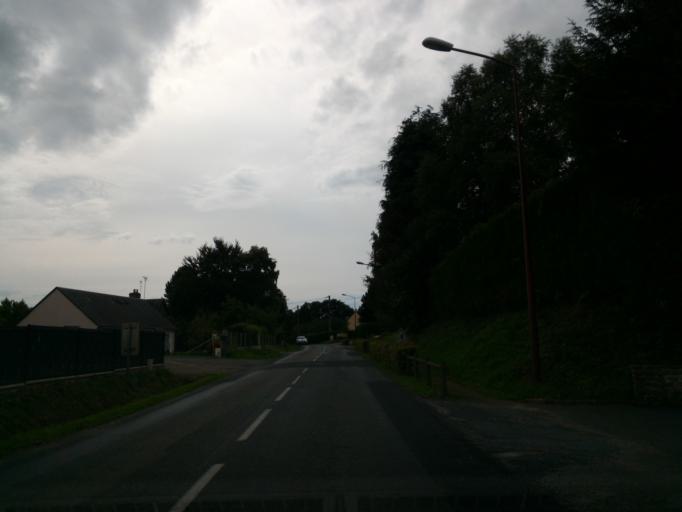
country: FR
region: Lower Normandy
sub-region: Departement de la Manche
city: La Haye-Pesnel
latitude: 48.7911
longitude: -1.4049
